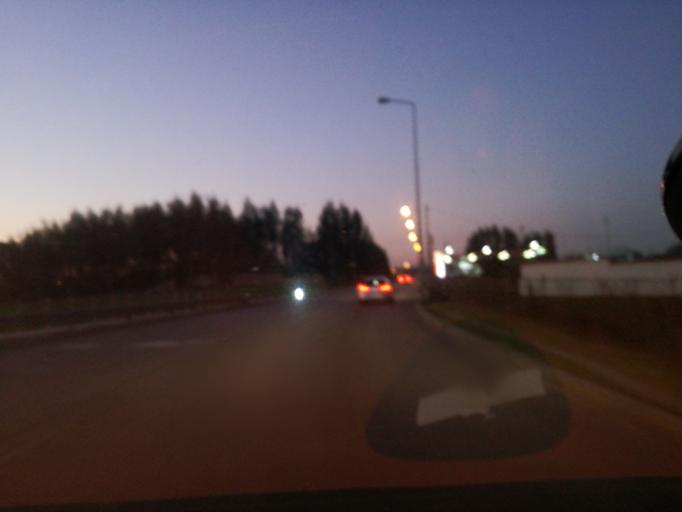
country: PT
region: Porto
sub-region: Valongo
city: Ermesinde
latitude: 41.2222
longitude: -8.5639
